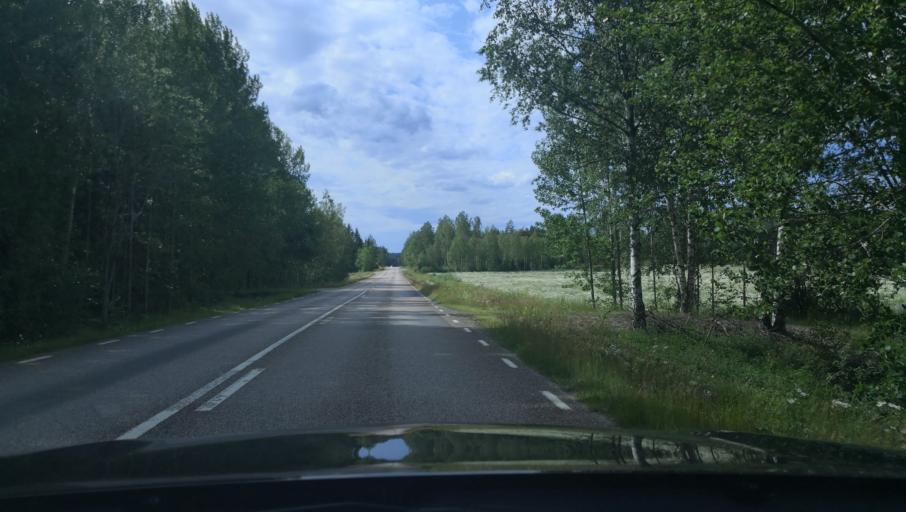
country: SE
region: Dalarna
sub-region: Avesta Kommun
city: Avesta
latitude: 59.9668
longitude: 16.1793
